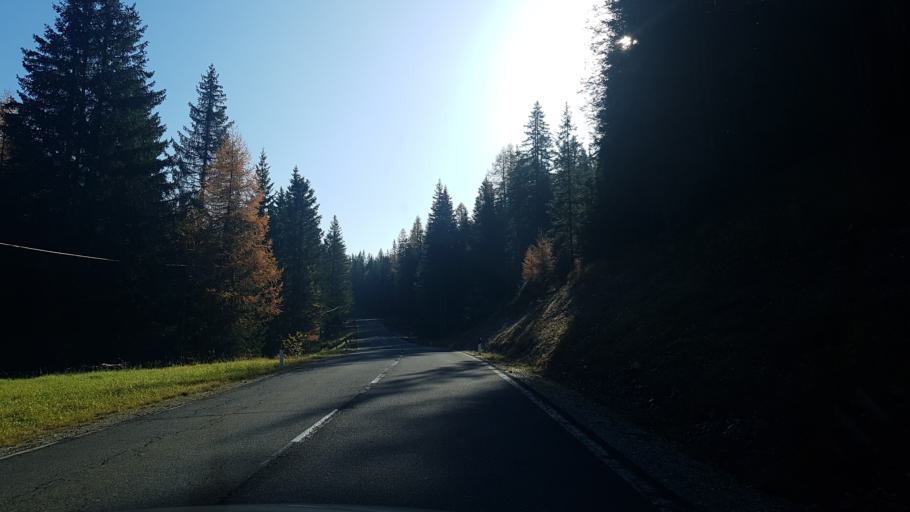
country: IT
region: Trentino-Alto Adige
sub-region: Bolzano
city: Sesto
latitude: 46.6723
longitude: 12.3889
